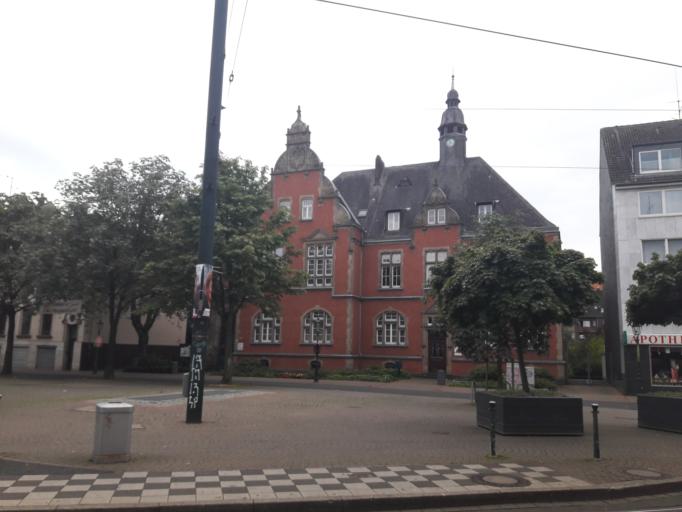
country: DE
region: North Rhine-Westphalia
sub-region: Regierungsbezirk Dusseldorf
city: Dusseldorf
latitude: 51.2013
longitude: 6.8381
